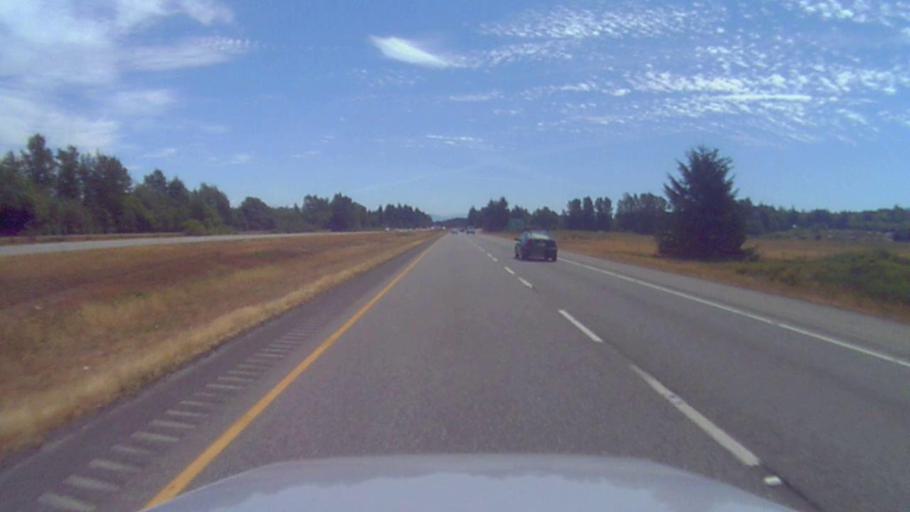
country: US
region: Washington
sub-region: Whatcom County
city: Ferndale
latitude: 48.8961
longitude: -122.6040
